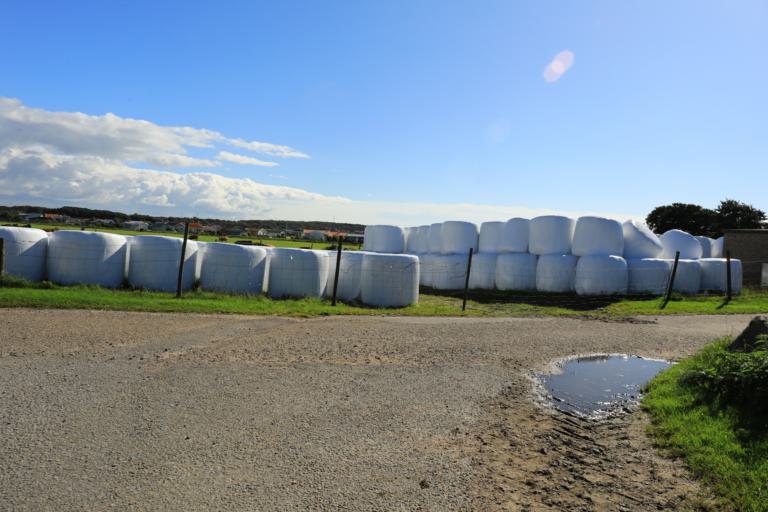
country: SE
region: Halland
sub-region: Varbergs Kommun
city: Traslovslage
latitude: 57.0722
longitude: 12.2681
